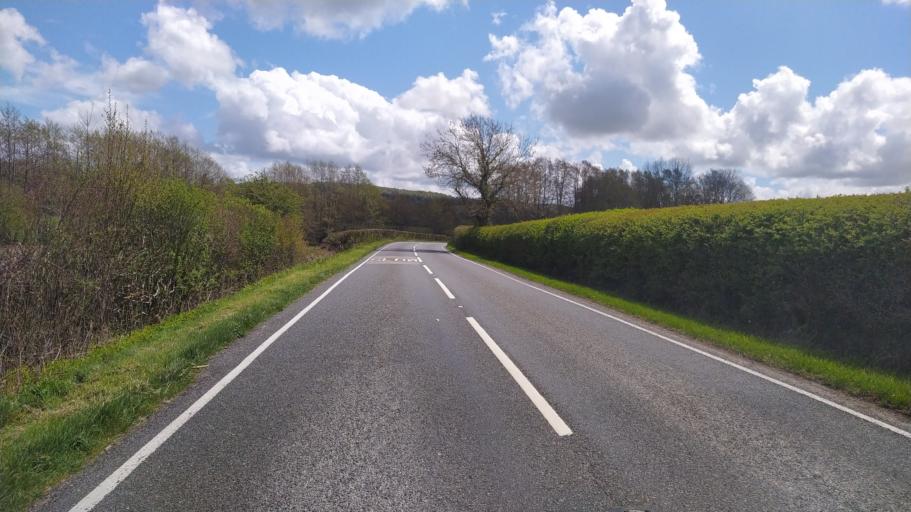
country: GB
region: England
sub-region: Somerset
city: Frome
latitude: 51.1792
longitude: -2.3103
